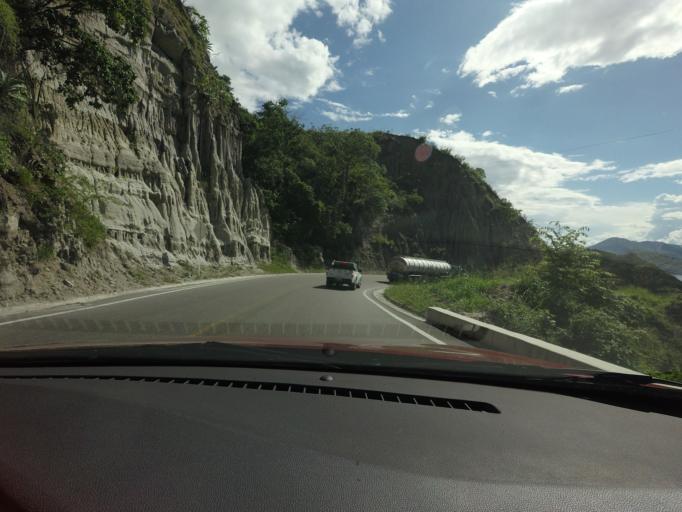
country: CO
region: Huila
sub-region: Gigante
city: Gigante
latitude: 2.4464
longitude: -75.5324
